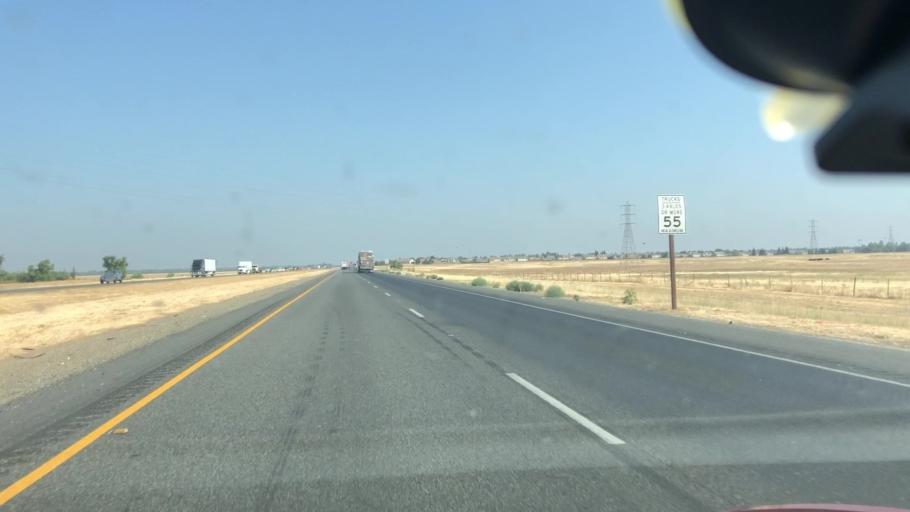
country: US
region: California
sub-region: Sacramento County
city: Laguna
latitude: 38.3849
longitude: -121.4786
